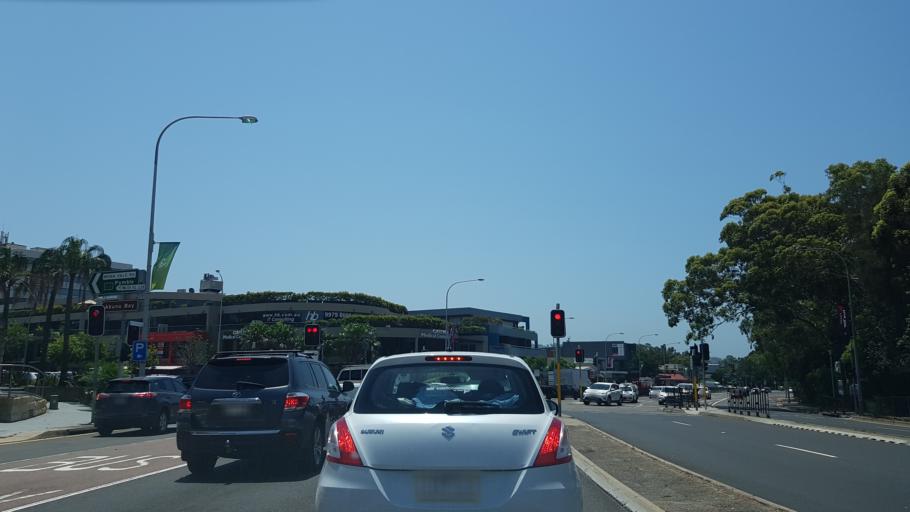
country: AU
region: New South Wales
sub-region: Pittwater
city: Warriewood
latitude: -33.6797
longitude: 151.3027
